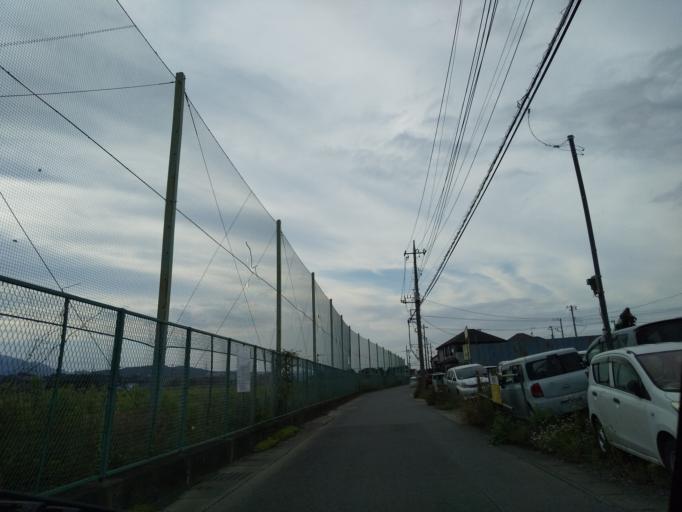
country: JP
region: Kanagawa
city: Zama
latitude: 35.4753
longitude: 139.3599
